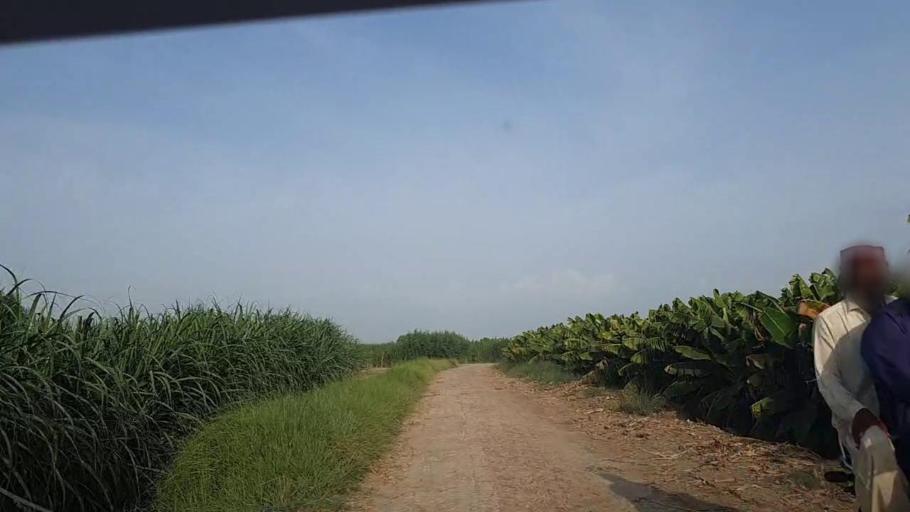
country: PK
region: Sindh
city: Ghotki
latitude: 27.9796
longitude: 69.2586
